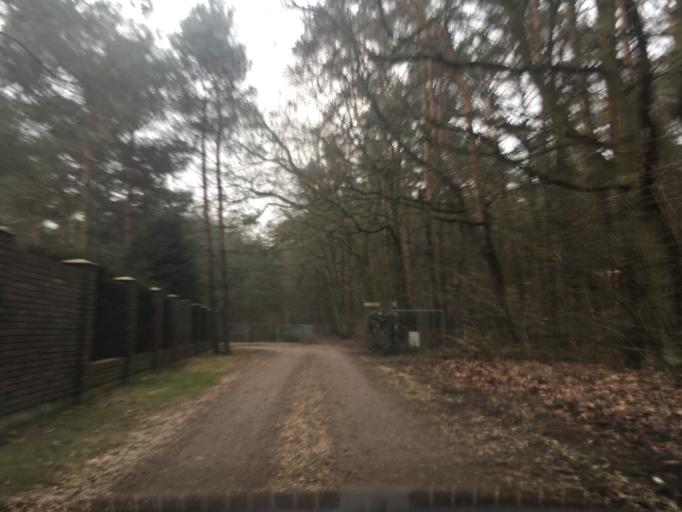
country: PL
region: Masovian Voivodeship
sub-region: Powiat piaseczynski
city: Lesznowola
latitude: 52.0753
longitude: 20.9173
